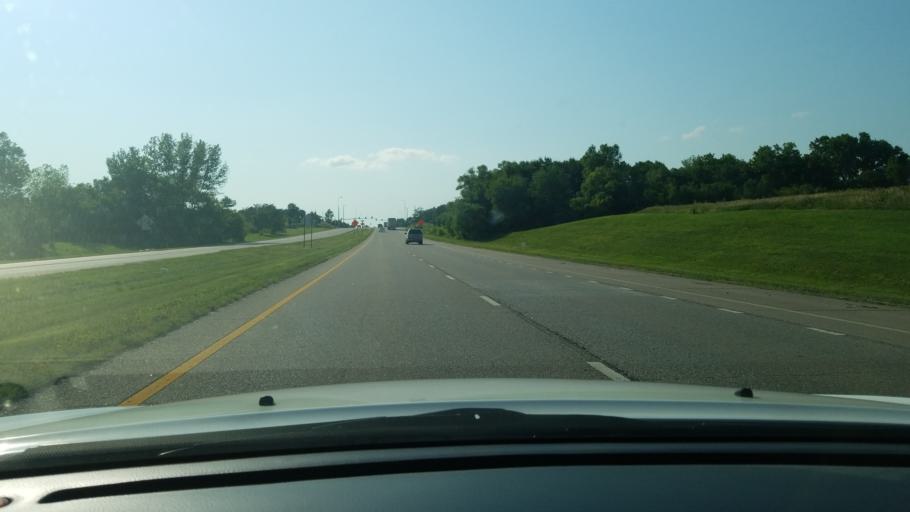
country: US
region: Nebraska
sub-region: Lancaster County
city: Lincoln
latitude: 40.7436
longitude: -96.6205
